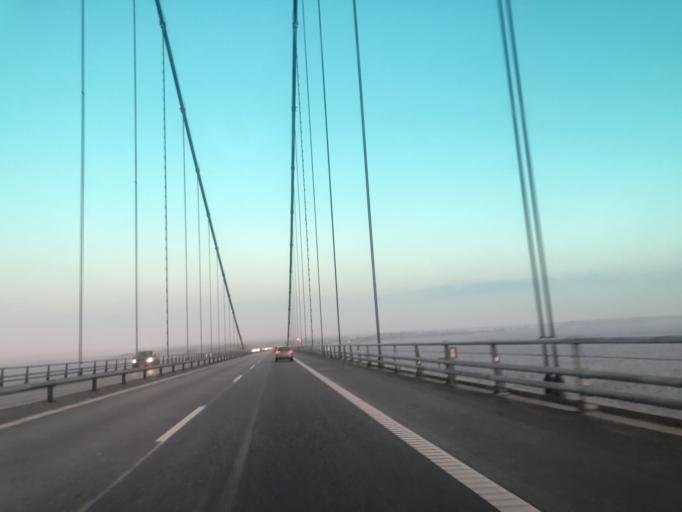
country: DK
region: Zealand
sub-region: Slagelse Kommune
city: Korsor
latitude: 55.3437
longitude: 11.0512
